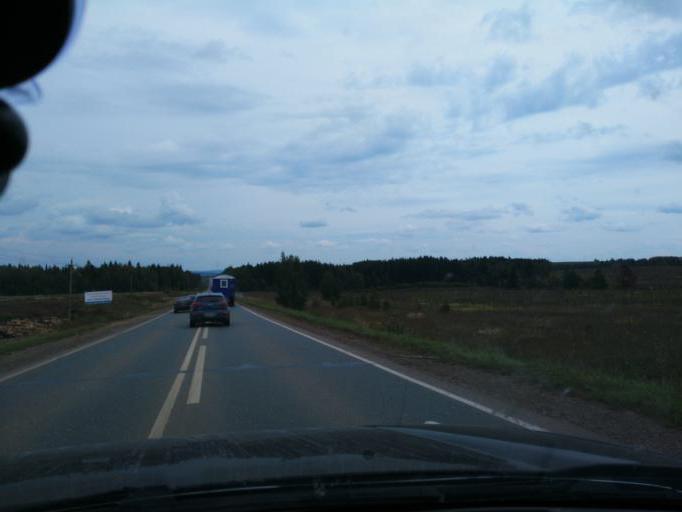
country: RU
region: Perm
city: Chernushka
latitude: 56.5099
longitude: 55.9192
